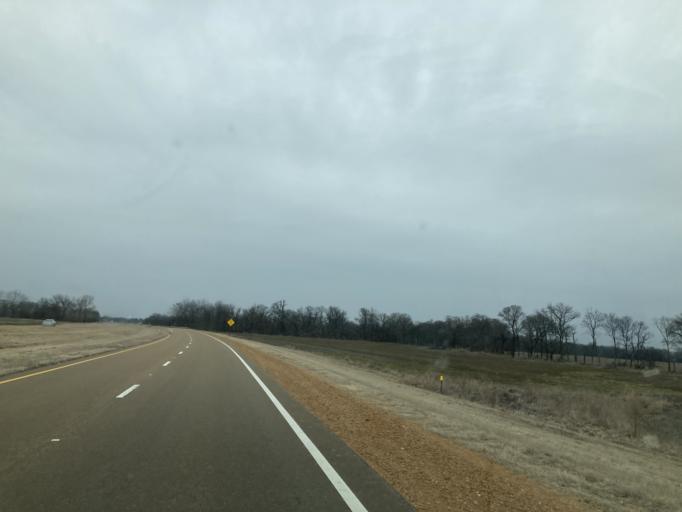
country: US
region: Mississippi
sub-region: Humphreys County
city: Belzoni
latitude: 33.0732
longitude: -90.4755
